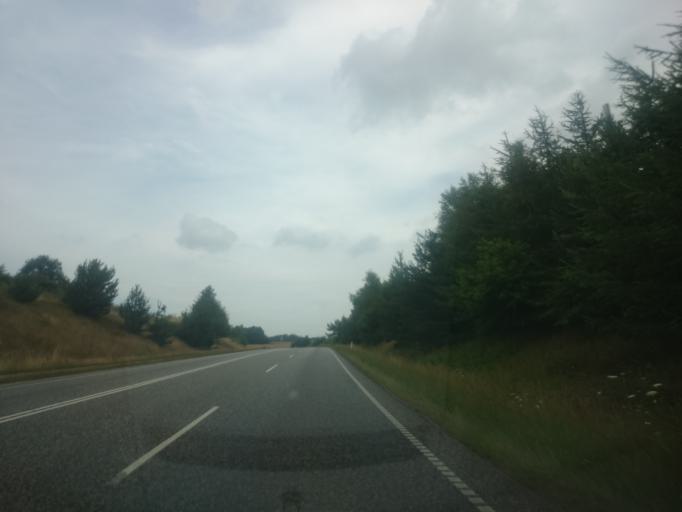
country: DK
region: South Denmark
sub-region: Vejle Kommune
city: Jelling
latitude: 55.6802
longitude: 9.3810
